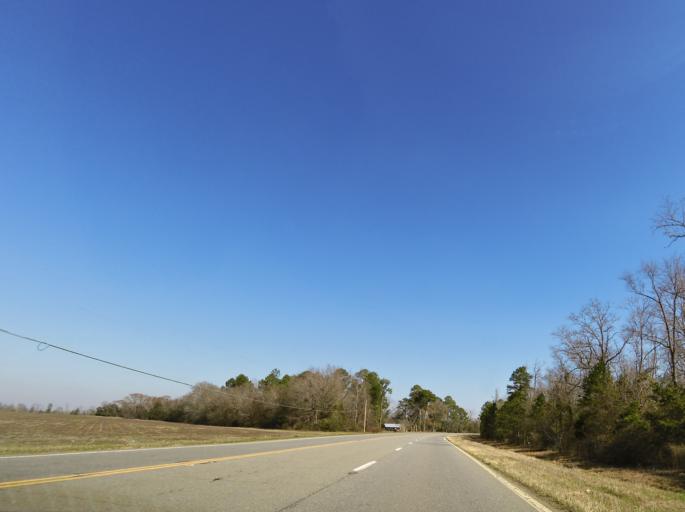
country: US
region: Georgia
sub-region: Bleckley County
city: Cochran
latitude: 32.3571
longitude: -83.3899
